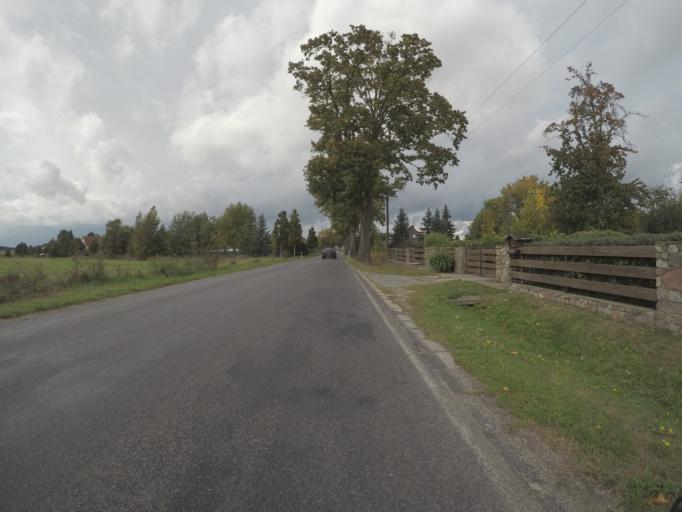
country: DE
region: Brandenburg
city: Werneuchen
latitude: 52.5968
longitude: 13.7667
